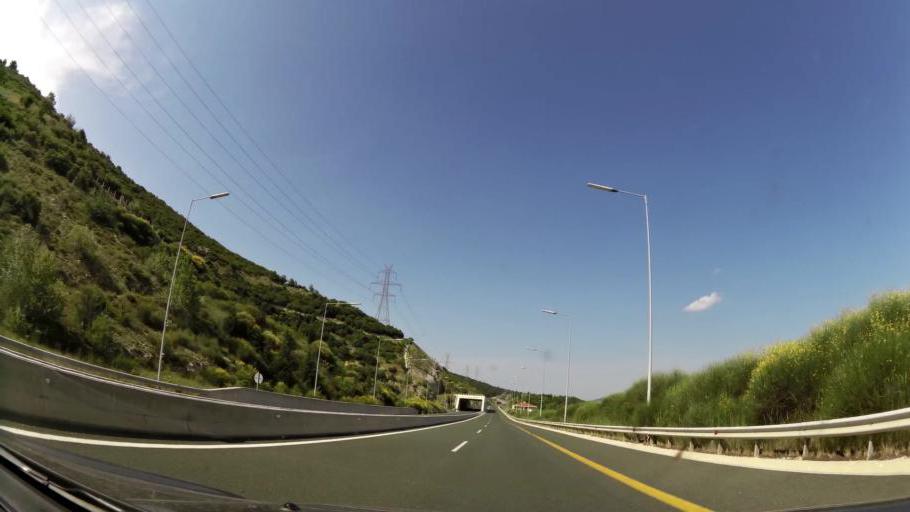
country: GR
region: Central Macedonia
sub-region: Nomos Imathias
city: Rizomata
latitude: 40.3930
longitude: 22.1581
